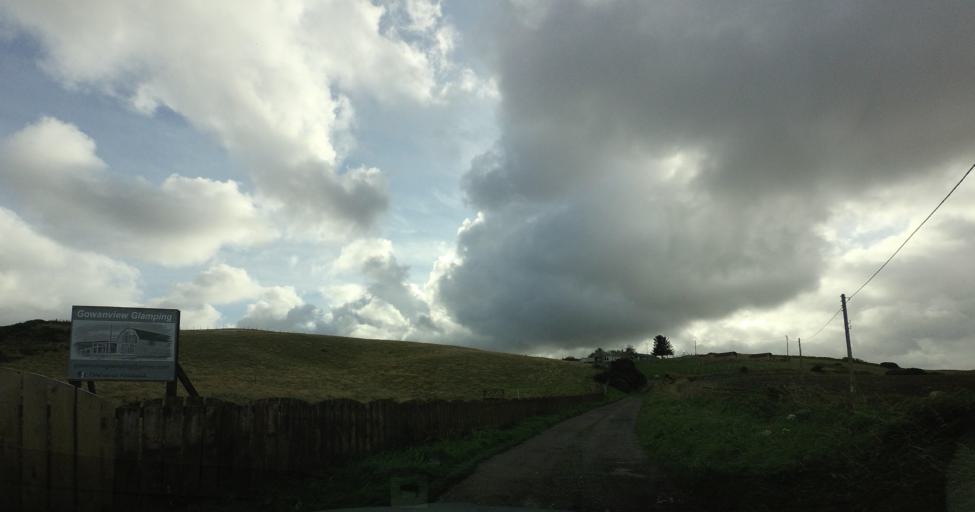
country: GB
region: Scotland
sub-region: Aberdeenshire
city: Banff
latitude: 57.6657
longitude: -2.5524
